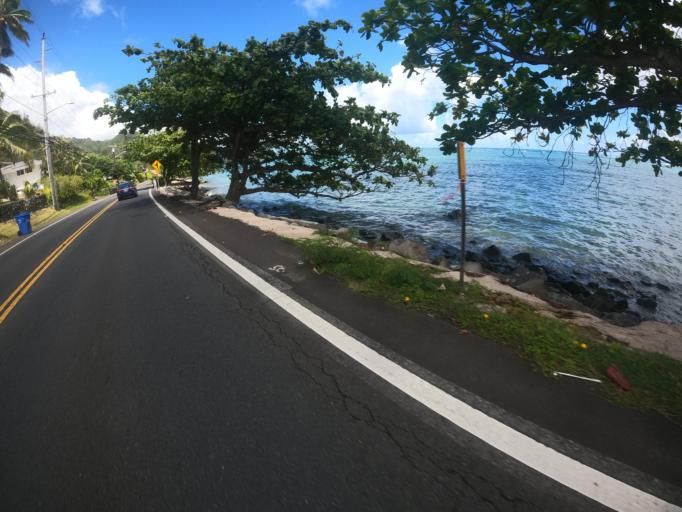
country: US
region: Hawaii
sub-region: Honolulu County
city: Ka'a'awa
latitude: 21.5588
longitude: -157.8598
